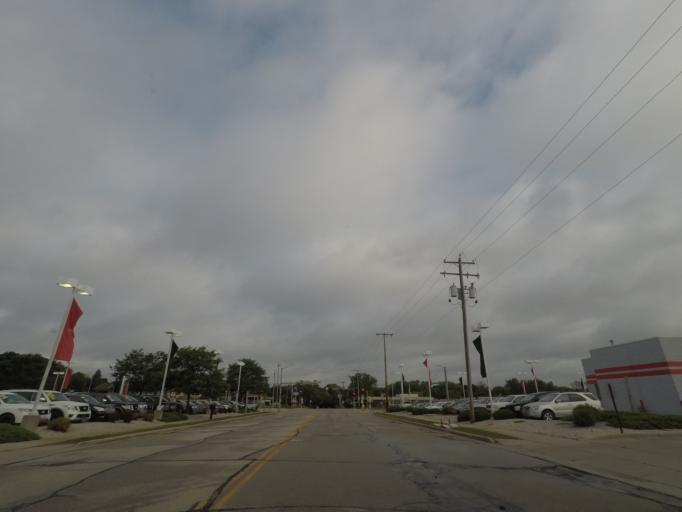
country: US
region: Wisconsin
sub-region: Waukesha County
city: Waukesha
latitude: 43.0238
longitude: -88.2068
